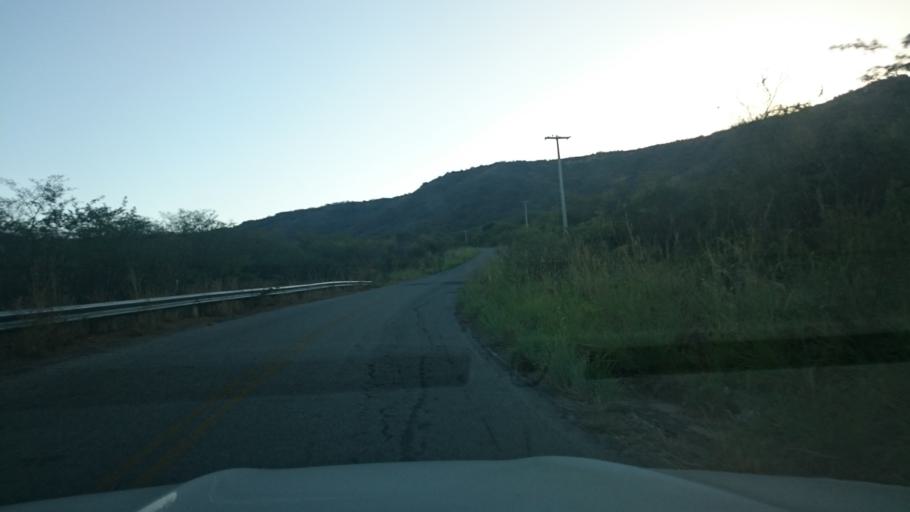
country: BR
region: Rio Grande do Norte
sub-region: Umarizal
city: Umarizal
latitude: -6.0087
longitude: -37.9797
